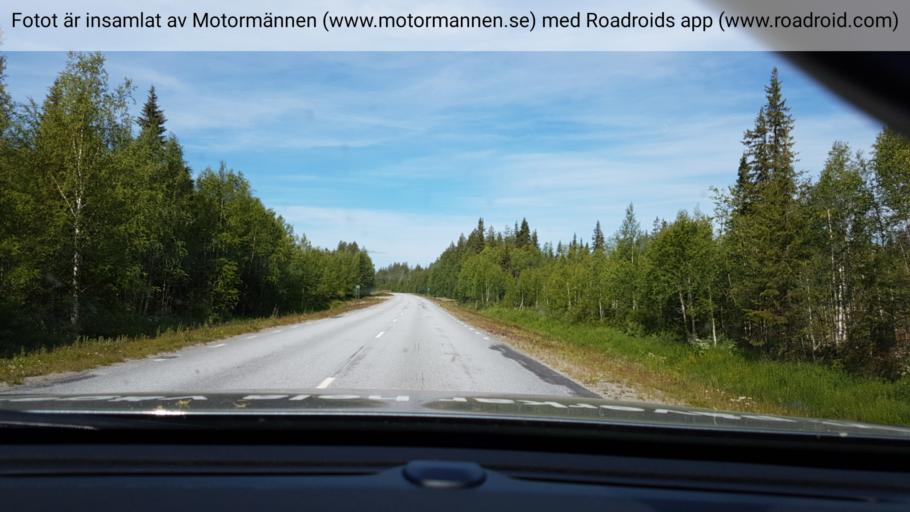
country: SE
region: Vaesterbotten
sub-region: Asele Kommun
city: Asele
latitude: 64.1842
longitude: 17.2455
